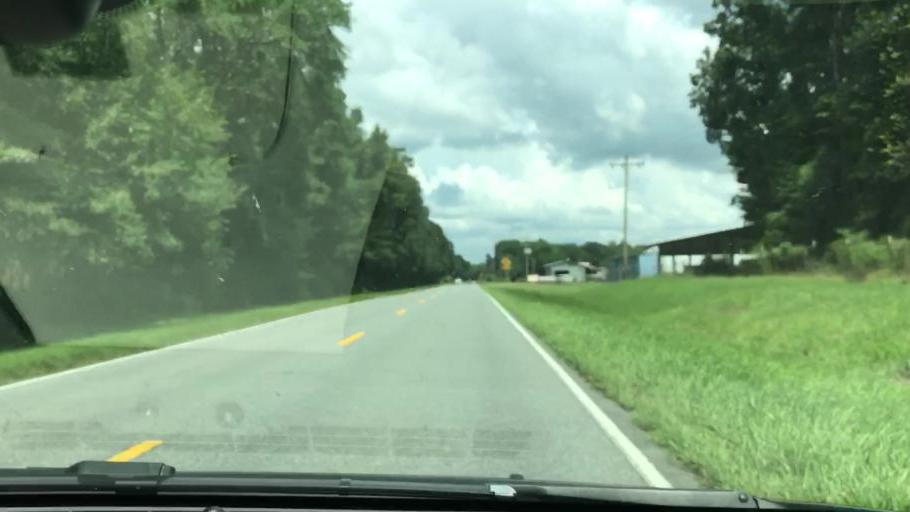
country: US
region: Florida
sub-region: Jackson County
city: Malone
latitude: 30.9029
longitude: -85.1311
